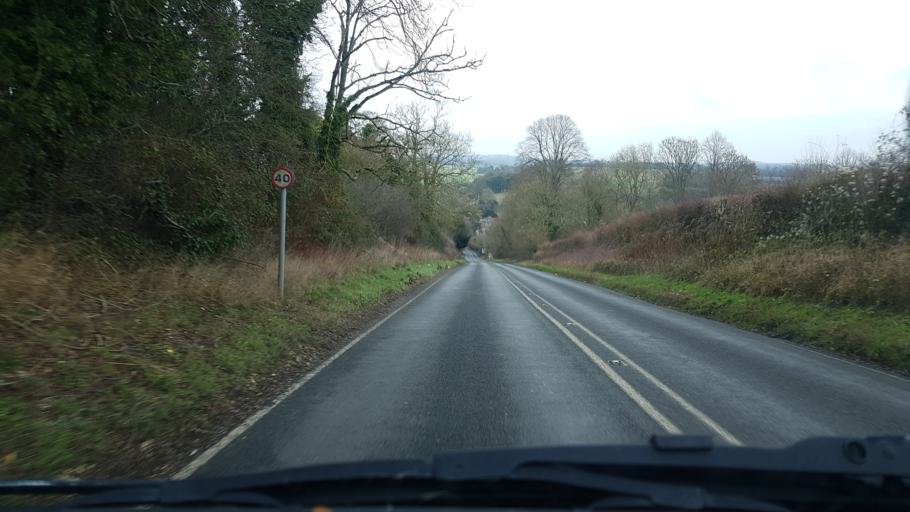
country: GB
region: England
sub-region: Hampshire
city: Andover
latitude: 51.2734
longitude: -1.4590
